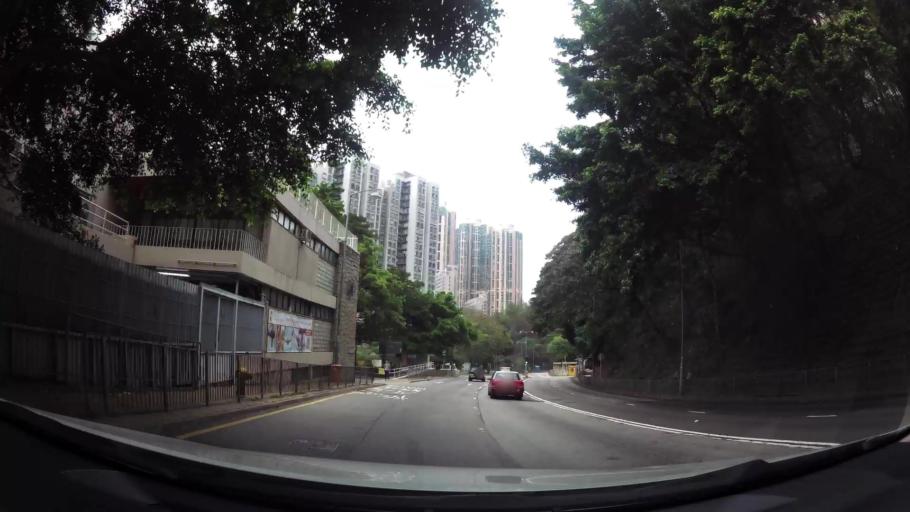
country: HK
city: Hong Kong
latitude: 22.2810
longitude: 114.1316
